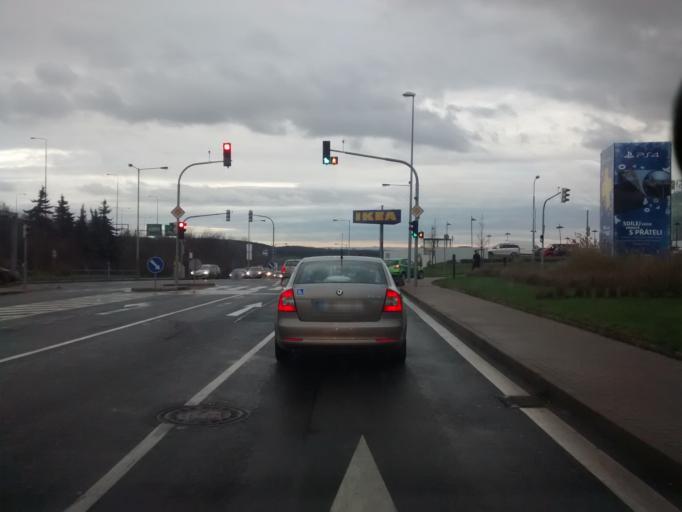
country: CZ
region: Praha
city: Cerny Most
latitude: 50.1074
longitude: 14.5876
